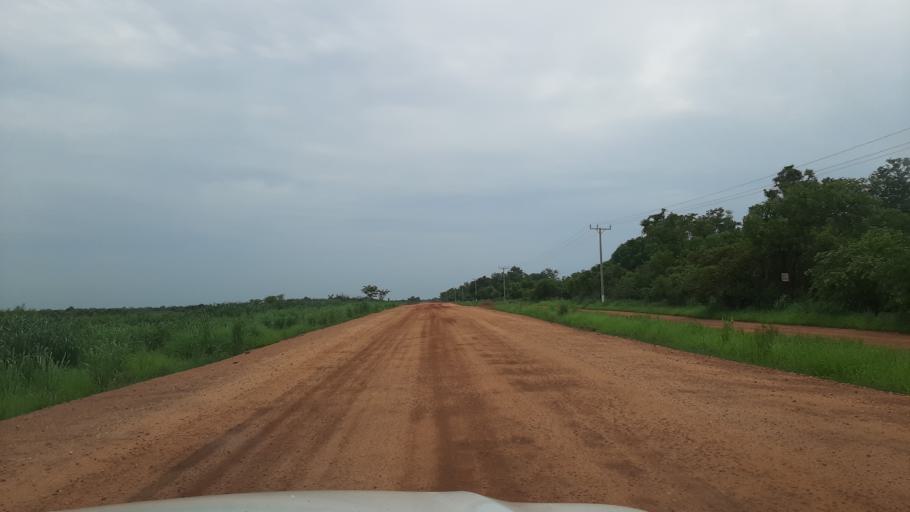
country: ET
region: Gambela
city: Gambela
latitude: 8.1592
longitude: 34.3082
